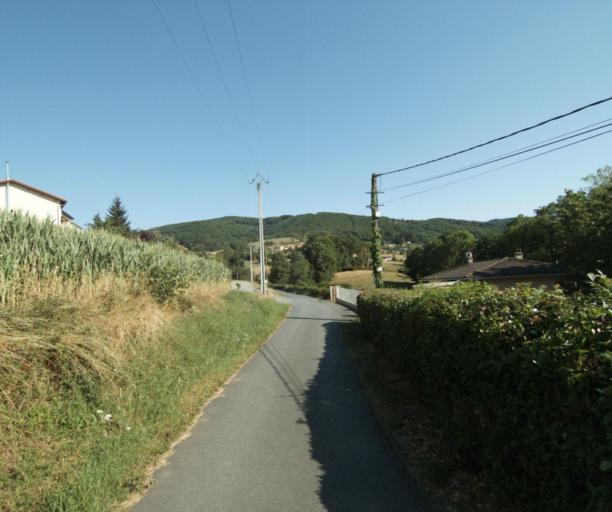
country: FR
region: Rhone-Alpes
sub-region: Departement du Rhone
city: Saint-Pierre-la-Palud
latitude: 45.7845
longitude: 4.6125
